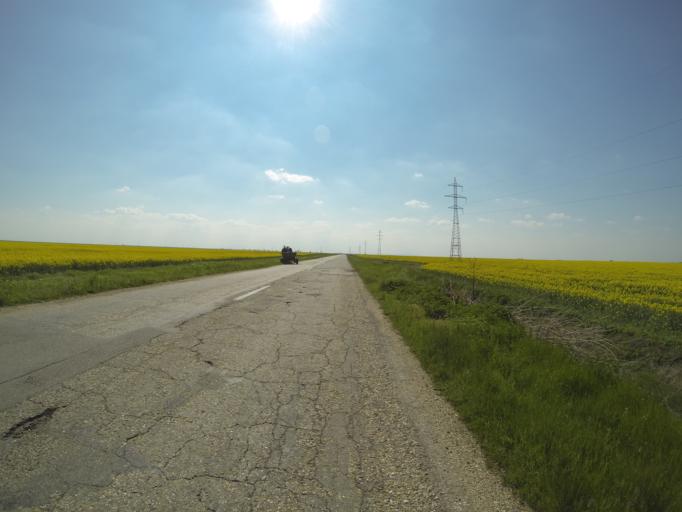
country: RO
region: Mehedinti
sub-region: Comuna Darvari
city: Gemeni
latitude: 44.1499
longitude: 23.1090
